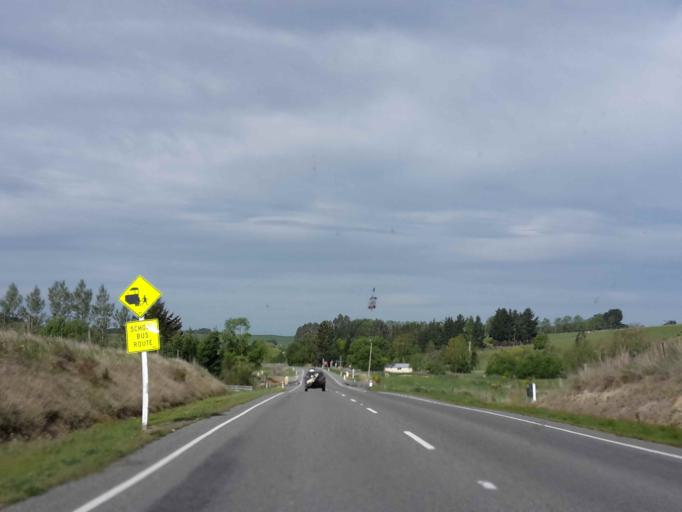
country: NZ
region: Canterbury
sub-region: Timaru District
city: Pleasant Point
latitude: -44.1115
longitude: 171.1416
